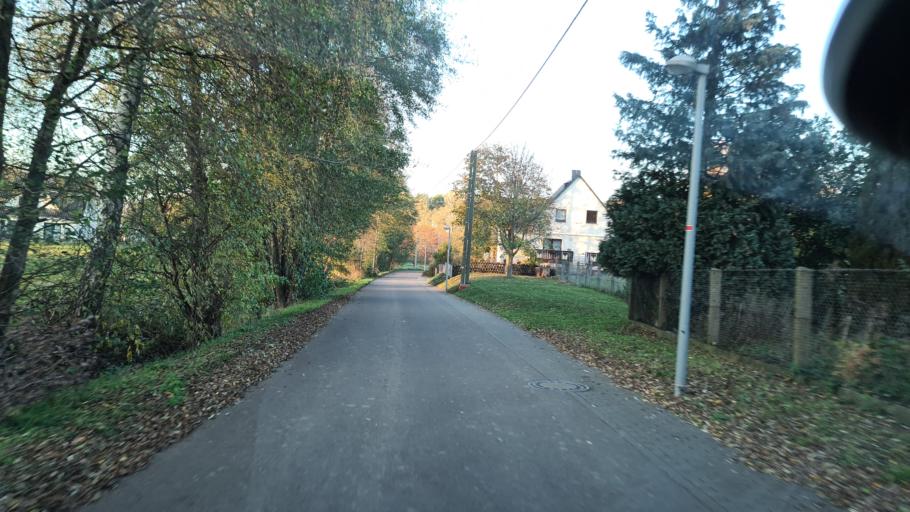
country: DE
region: Saxony
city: Schildau
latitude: 51.4316
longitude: 12.9746
